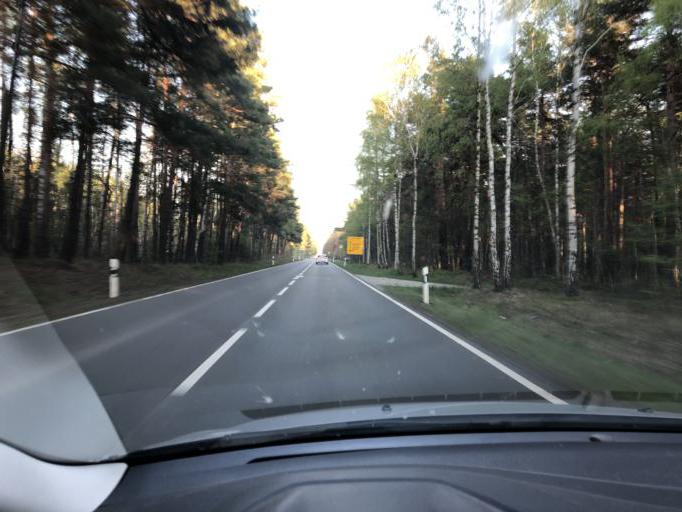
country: DE
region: Brandenburg
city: Welzow
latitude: 51.5385
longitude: 14.1887
